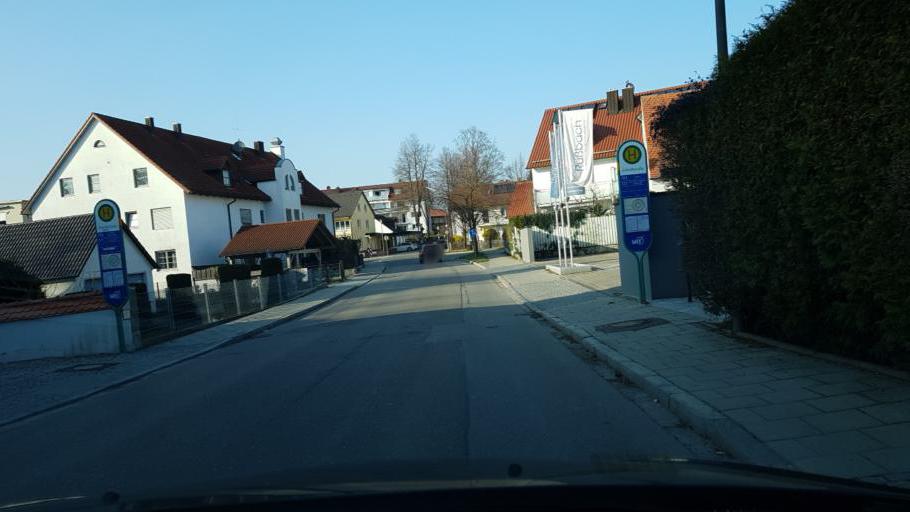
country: DE
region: Bavaria
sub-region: Upper Bavaria
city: Odelzhausen
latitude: 48.3102
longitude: 11.1989
